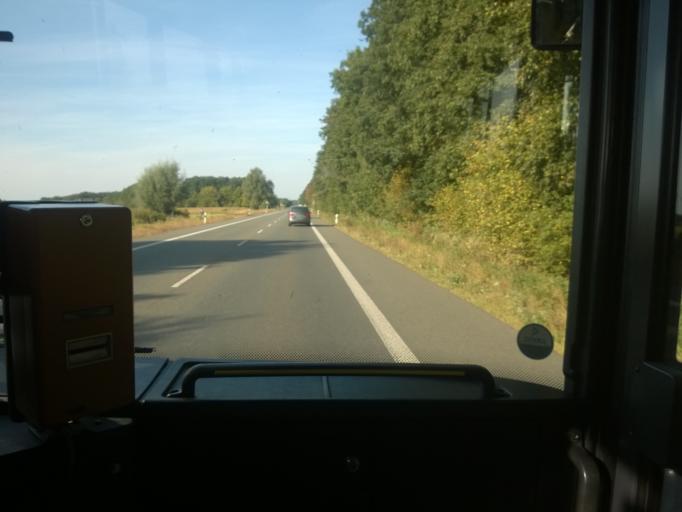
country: DE
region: North Rhine-Westphalia
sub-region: Regierungsbezirk Munster
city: Borken
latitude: 51.8745
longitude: 6.8588
